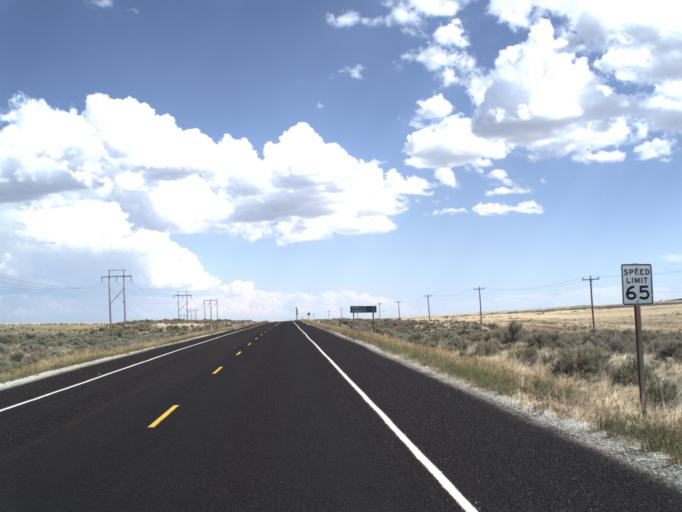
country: US
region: Idaho
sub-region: Minidoka County
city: Rupert
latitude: 41.9971
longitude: -113.1926
